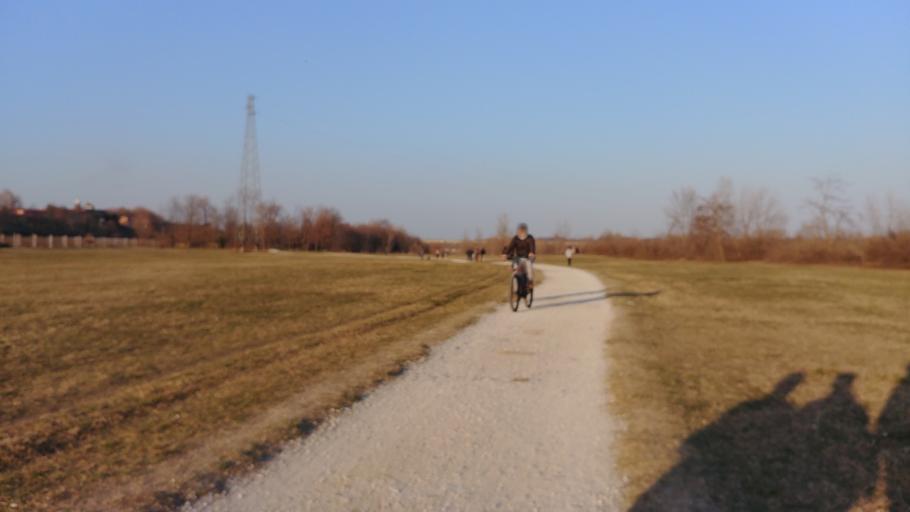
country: IT
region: Piedmont
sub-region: Provincia di Cuneo
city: Boves
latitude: 44.3581
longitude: 7.5338
